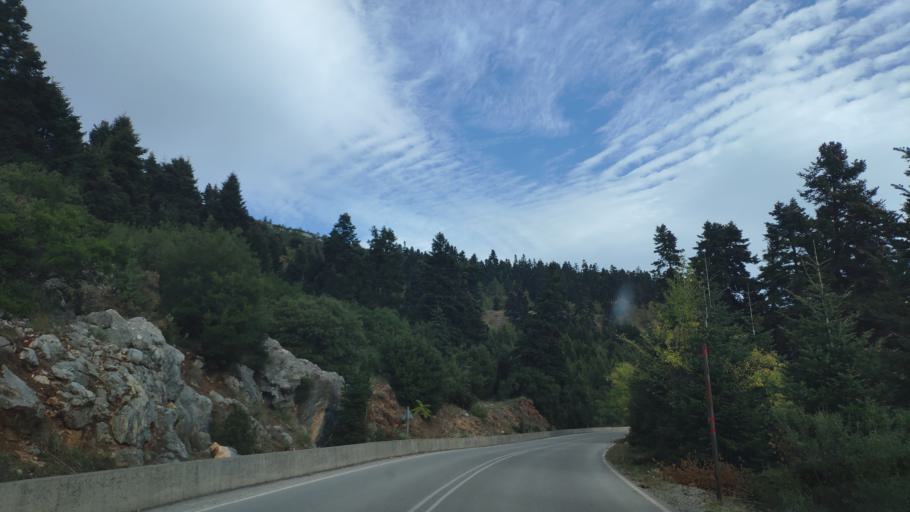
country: GR
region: Central Greece
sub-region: Nomos Fokidos
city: Amfissa
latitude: 38.6390
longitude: 22.3821
